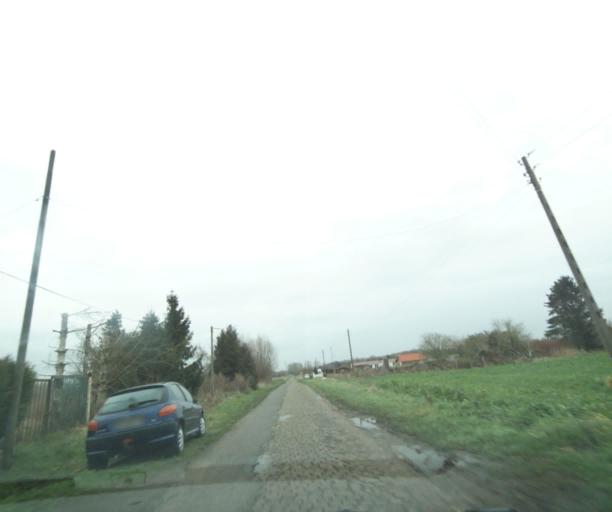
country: FR
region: Nord-Pas-de-Calais
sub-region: Departement du Nord
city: Fresnes-sur-Escaut
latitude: 50.4210
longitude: 3.5888
